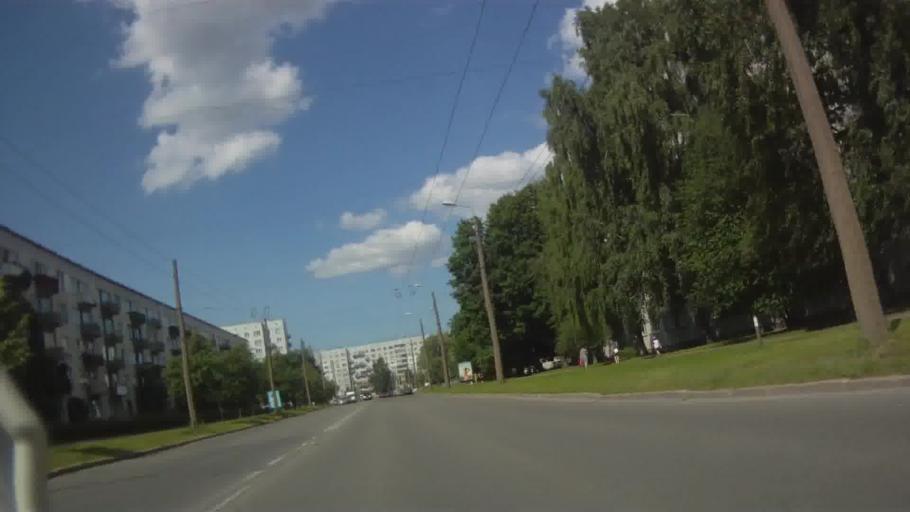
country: LV
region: Riga
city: Riga
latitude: 56.9564
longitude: 24.1762
